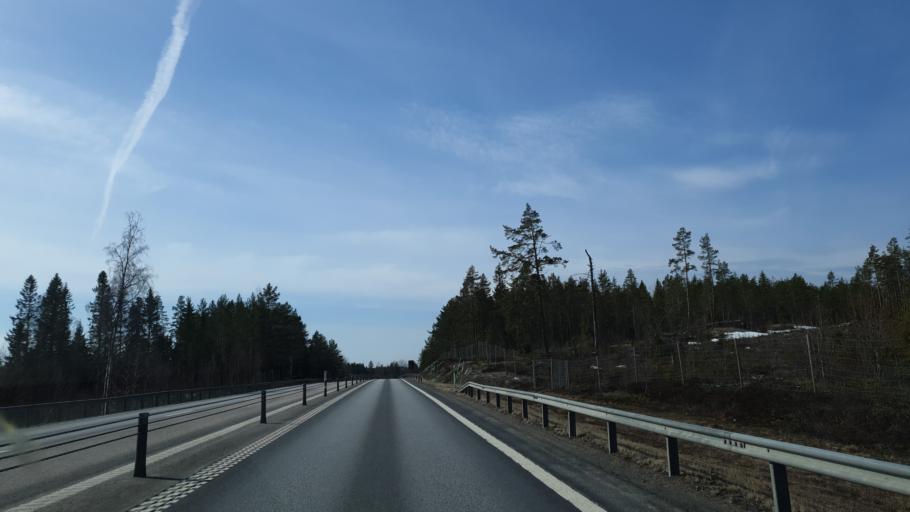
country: SE
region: Vaesterbotten
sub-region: Nordmalings Kommun
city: Nordmaling
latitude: 63.5084
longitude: 19.3519
